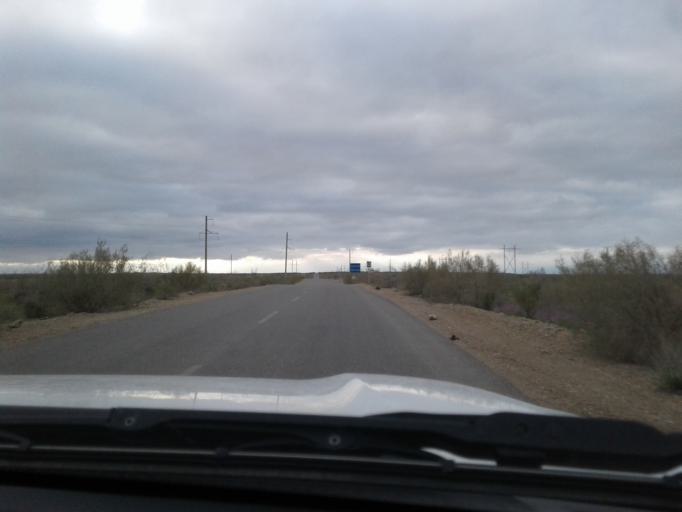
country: TM
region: Lebap
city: Sayat
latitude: 38.9212
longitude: 64.2875
